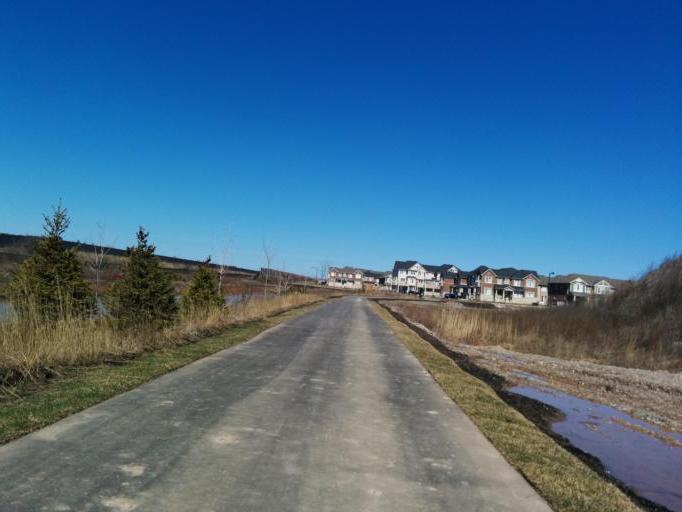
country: CA
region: Ontario
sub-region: Halton
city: Milton
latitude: 43.4859
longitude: -79.8632
